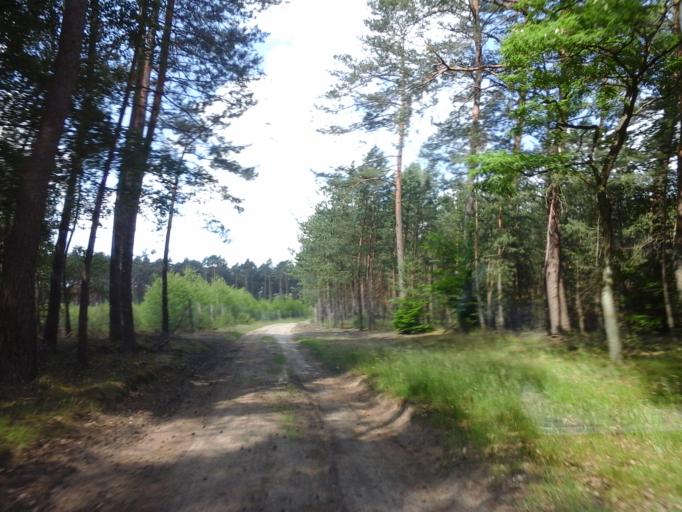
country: PL
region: West Pomeranian Voivodeship
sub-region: Powiat choszczenski
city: Bierzwnik
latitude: 53.0930
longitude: 15.7339
